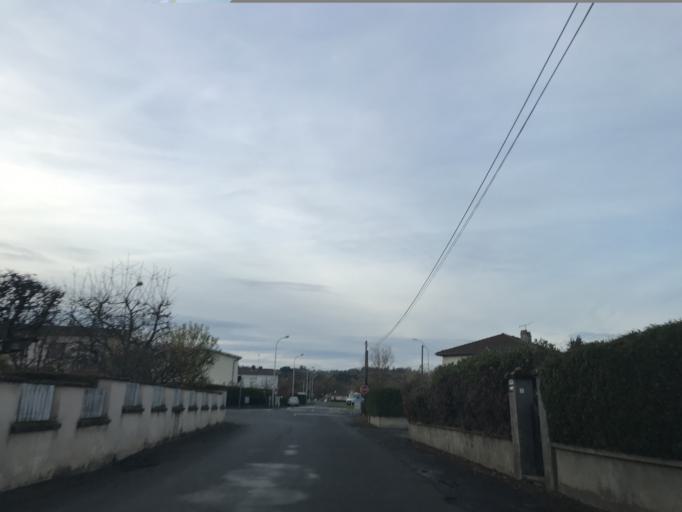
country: FR
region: Auvergne
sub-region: Departement du Puy-de-Dome
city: Courpiere
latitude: 45.7606
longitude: 3.5377
